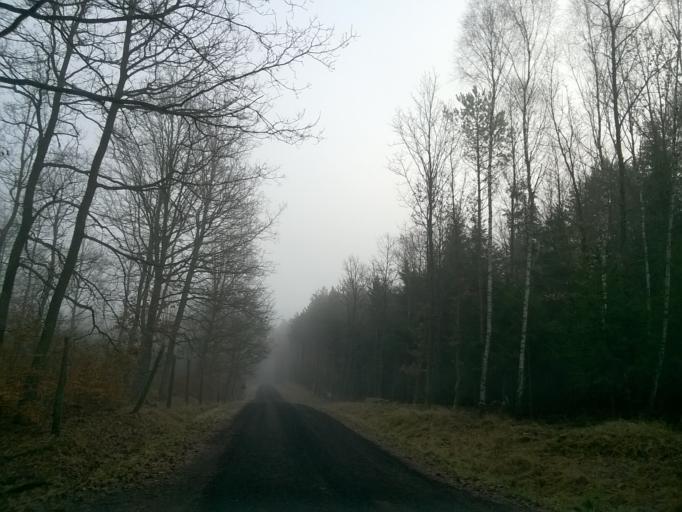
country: PL
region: Kujawsko-Pomorskie
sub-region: Powiat nakielski
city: Kcynia
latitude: 53.0419
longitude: 17.5049
